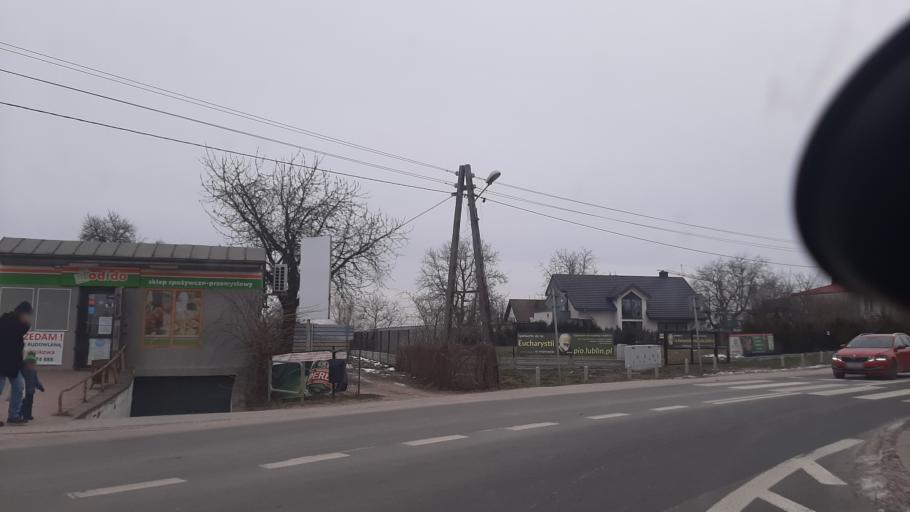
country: PL
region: Lublin Voivodeship
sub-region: Powiat lubelski
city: Lublin
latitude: 51.2776
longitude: 22.5814
